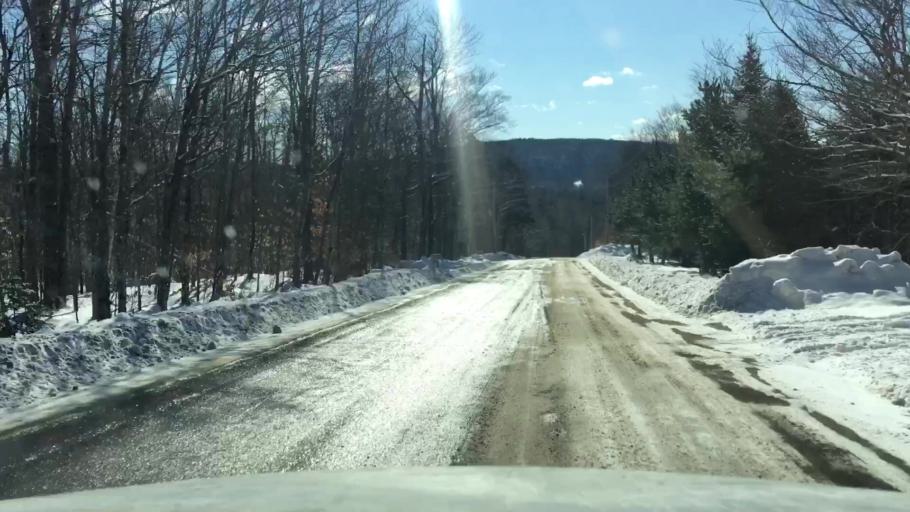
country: US
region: Maine
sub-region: Washington County
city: Calais
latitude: 45.0733
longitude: -67.5006
